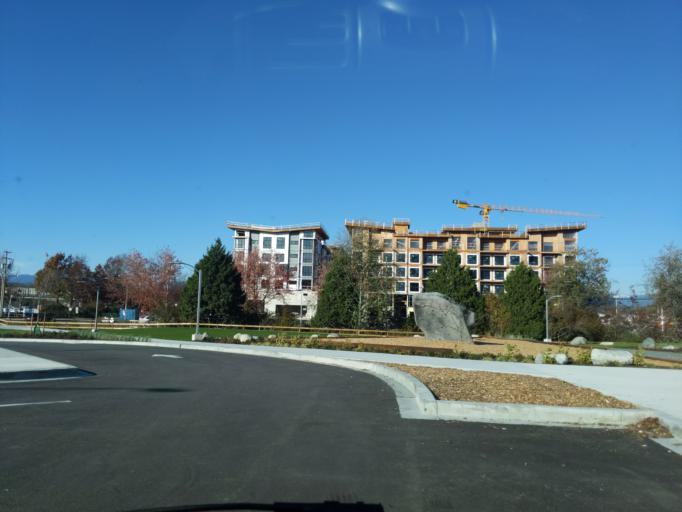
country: CA
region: British Columbia
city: New Westminster
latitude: 49.2018
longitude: -122.8714
